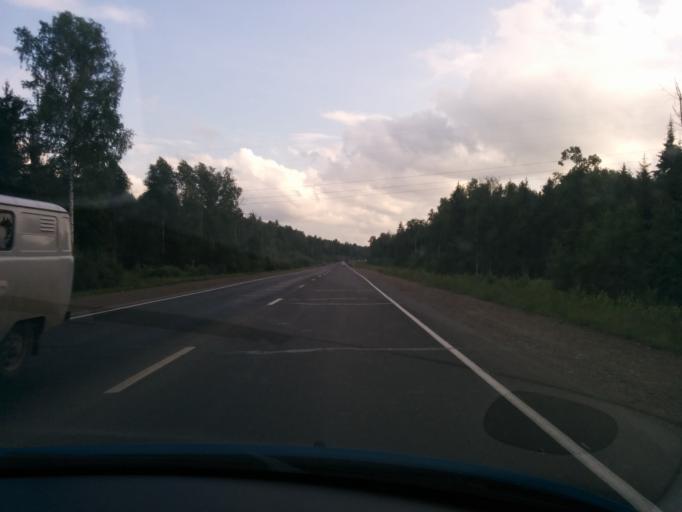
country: RU
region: Perm
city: Novyye Lyady
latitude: 58.0772
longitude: 56.4313
